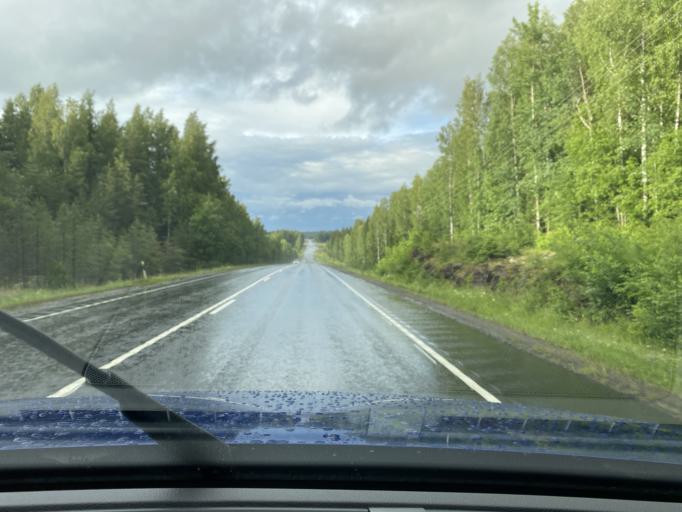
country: FI
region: Uusimaa
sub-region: Helsinki
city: Nurmijaervi
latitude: 60.4649
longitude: 24.8359
